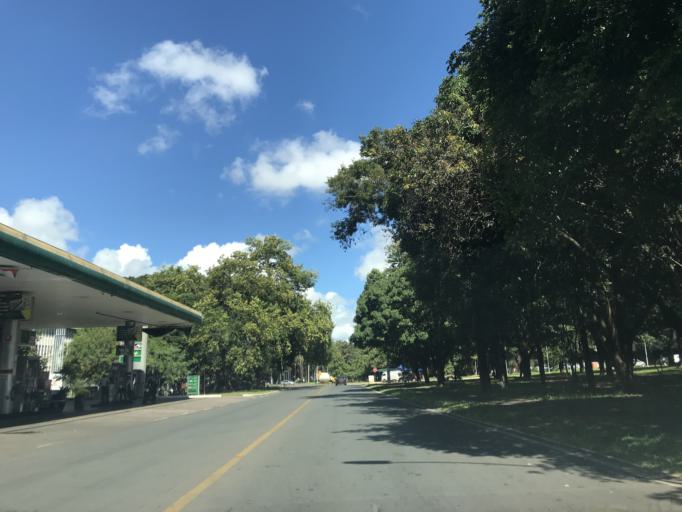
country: BR
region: Federal District
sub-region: Brasilia
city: Brasilia
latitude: -15.8228
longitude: -47.9030
